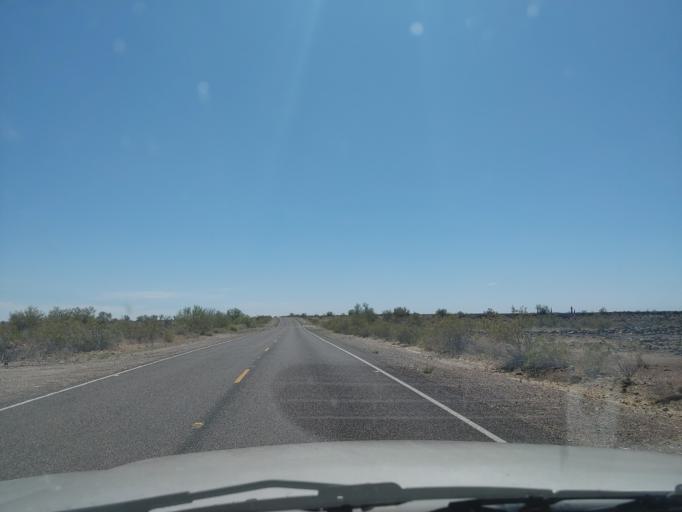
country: US
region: Arizona
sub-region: Maricopa County
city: Gila Bend
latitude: 32.9273
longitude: -113.2942
